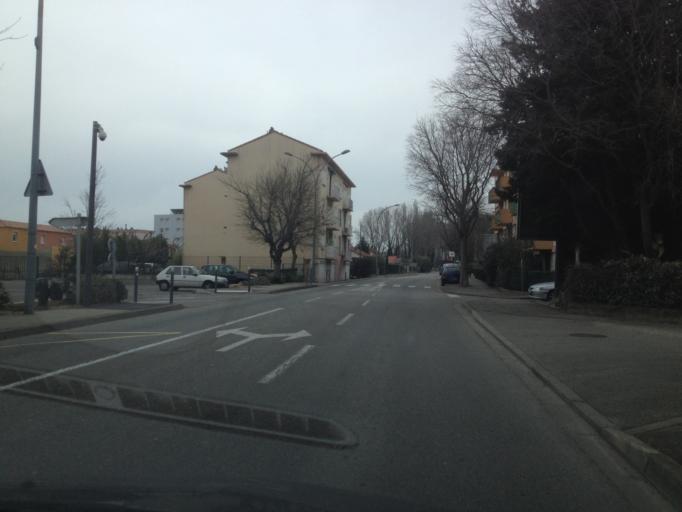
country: FR
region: Provence-Alpes-Cote d'Azur
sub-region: Departement du Vaucluse
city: Sorgues
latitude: 44.0045
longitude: 4.8769
